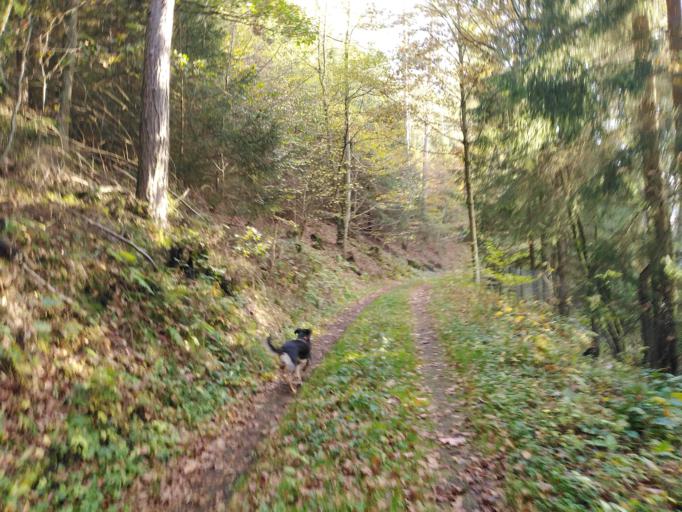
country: DE
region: North Rhine-Westphalia
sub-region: Regierungsbezirk Arnsberg
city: Brilon
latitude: 51.3635
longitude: 8.6209
